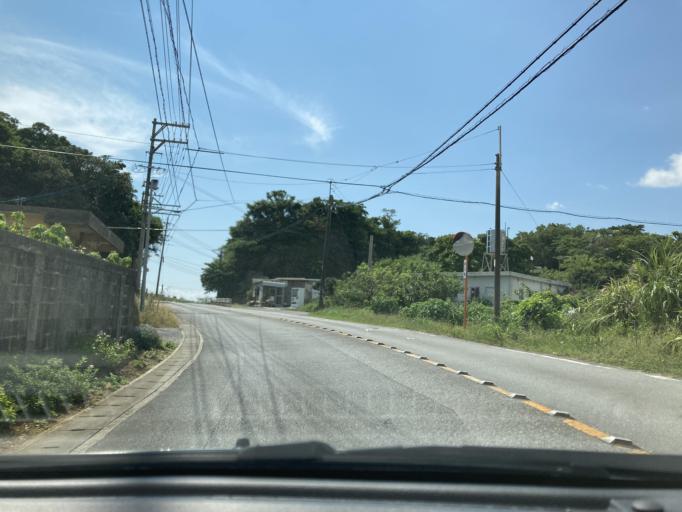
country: JP
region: Okinawa
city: Tomigusuku
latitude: 26.1483
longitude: 127.7909
